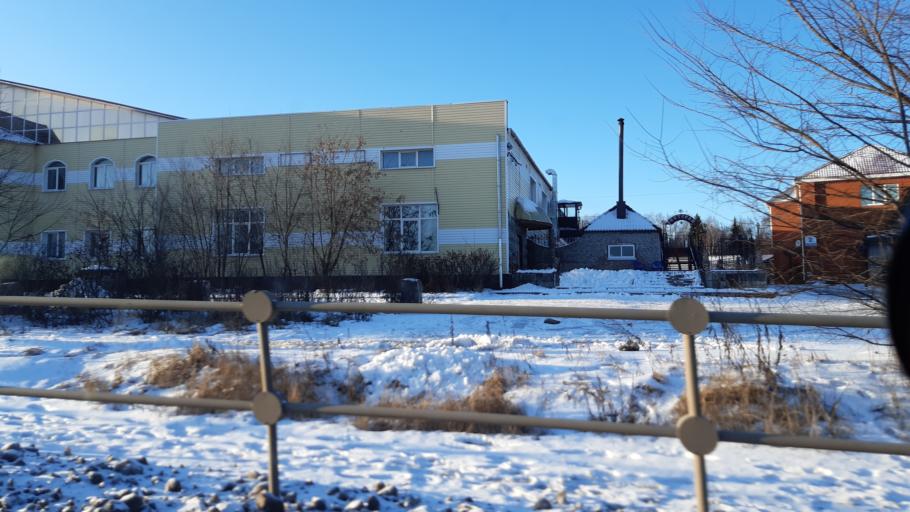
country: RU
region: Moskovskaya
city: Skoropuskovskiy
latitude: 56.3387
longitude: 38.1632
